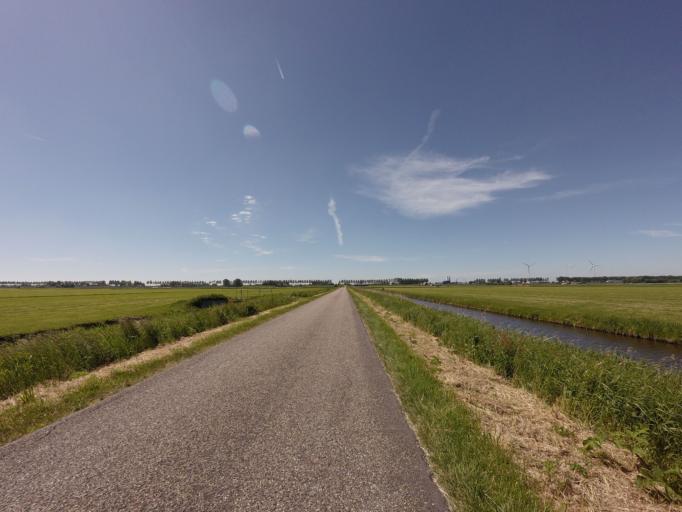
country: NL
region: North Holland
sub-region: Gemeente Alkmaar
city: Alkmaar
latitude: 52.5815
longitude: 4.7672
